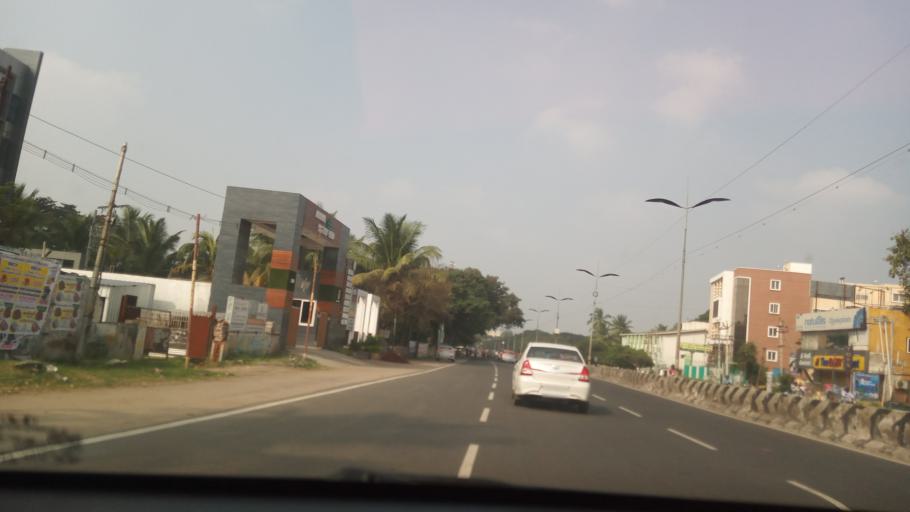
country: IN
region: Tamil Nadu
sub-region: Coimbatore
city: Singanallur
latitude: 11.0253
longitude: 77.0140
